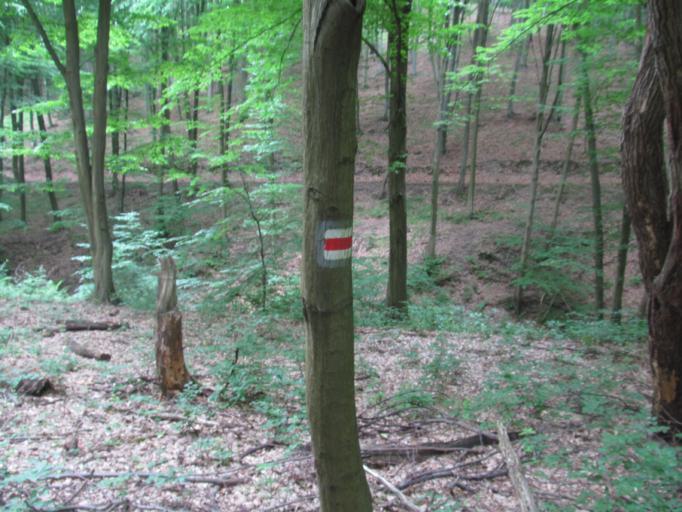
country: HU
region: Borsod-Abauj-Zemplen
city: Borsodnadasd
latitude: 48.1191
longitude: 20.1895
